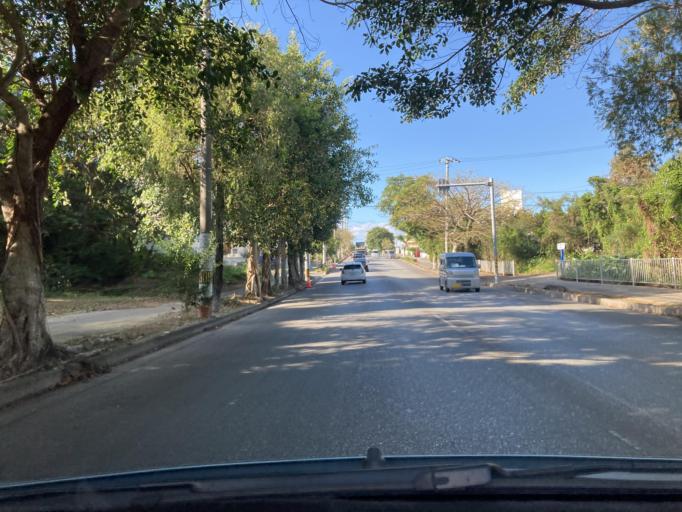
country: JP
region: Okinawa
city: Gushikawa
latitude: 26.3655
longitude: 127.8414
